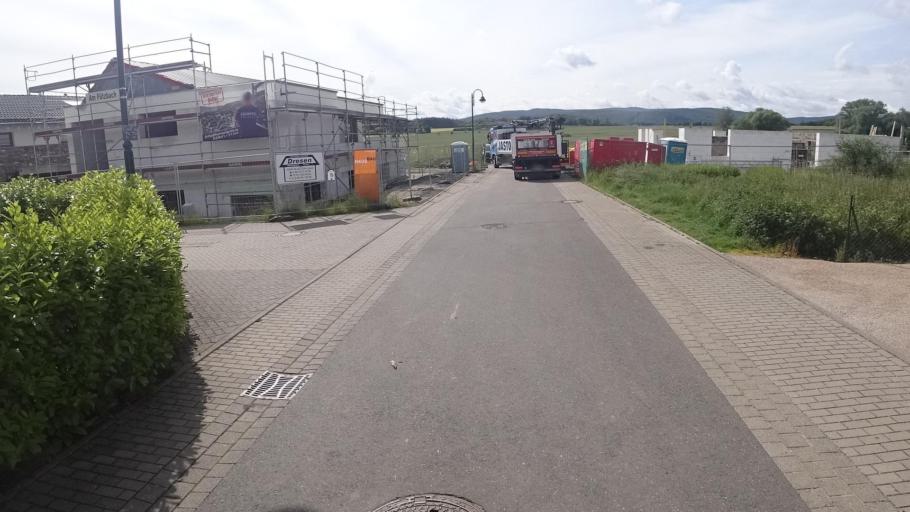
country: DE
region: Rheinland-Pfalz
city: Dernau
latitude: 50.5499
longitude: 7.0376
